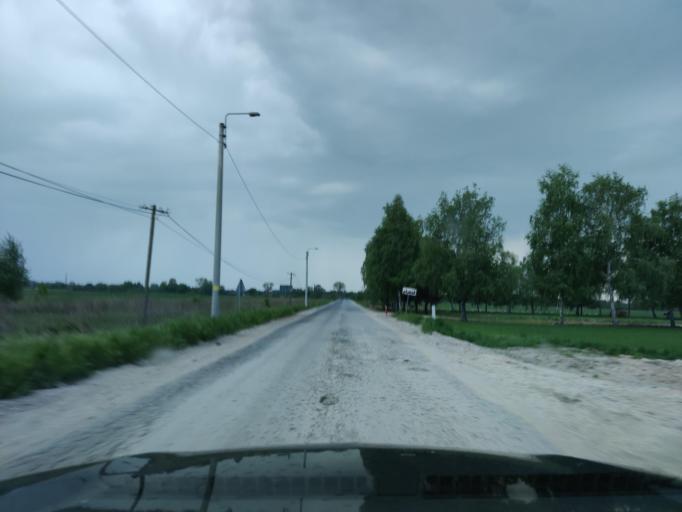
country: PL
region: Masovian Voivodeship
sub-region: Powiat piaseczynski
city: Konstancin-Jeziorna
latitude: 52.1218
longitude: 21.1495
